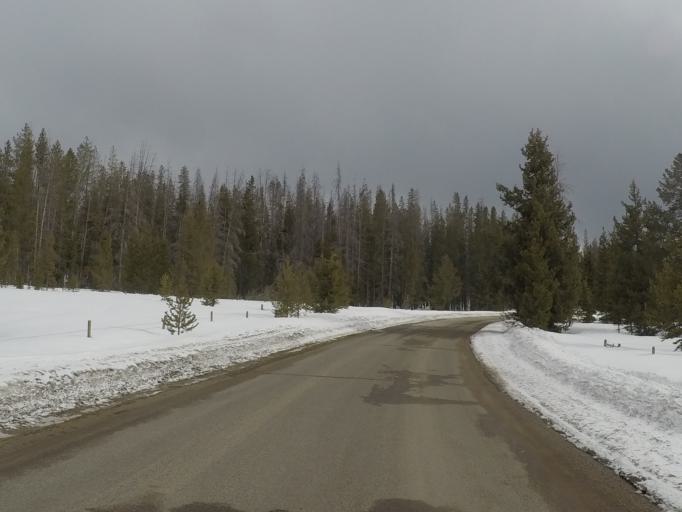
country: US
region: Montana
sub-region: Granite County
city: Philipsburg
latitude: 46.2086
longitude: -113.2512
